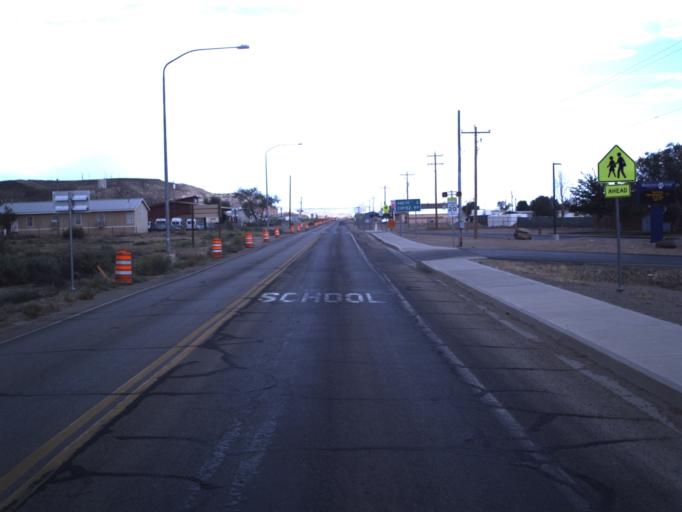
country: US
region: Utah
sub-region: San Juan County
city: Blanding
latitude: 37.2614
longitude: -109.3057
